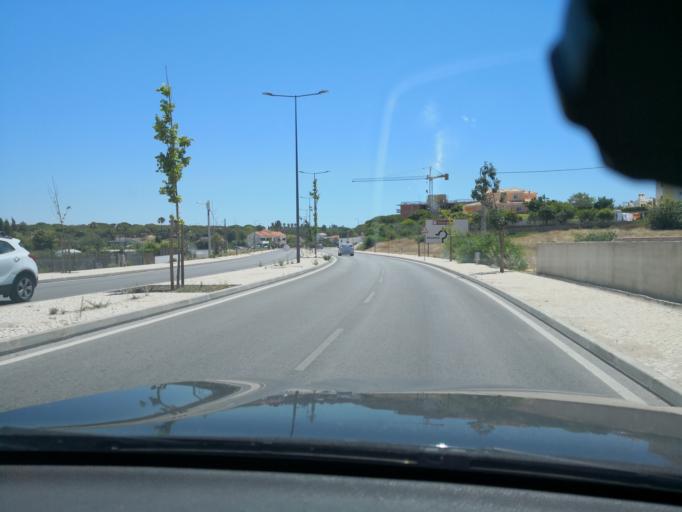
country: PT
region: Faro
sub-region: Loule
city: Quarteira
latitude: 37.0712
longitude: -8.0867
